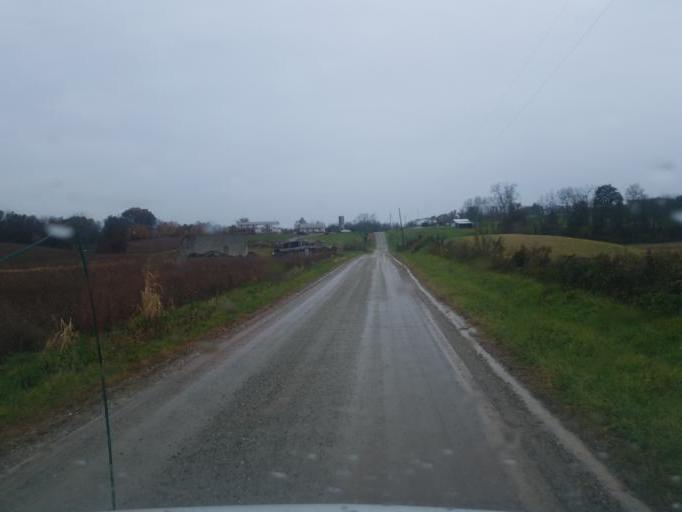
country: US
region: Ohio
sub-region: Washington County
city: Beverly
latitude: 39.4711
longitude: -81.6902
